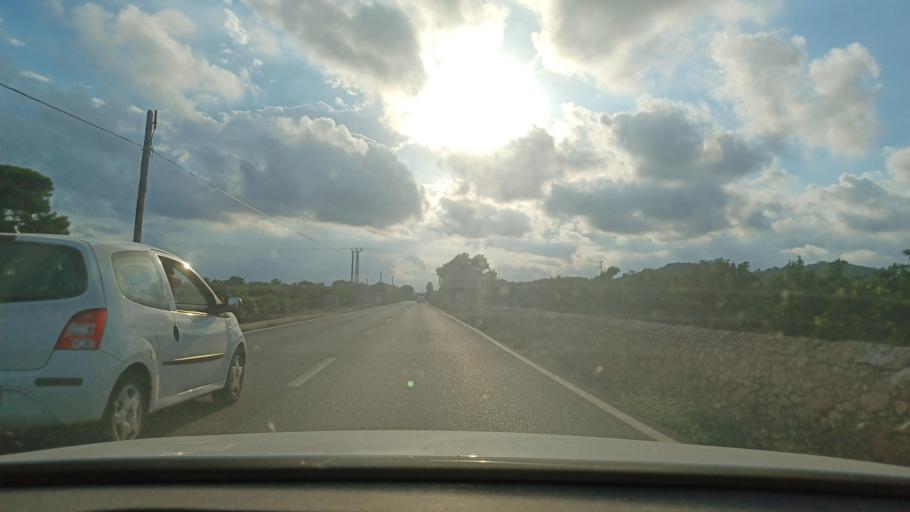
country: ES
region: Catalonia
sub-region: Provincia de Tarragona
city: Alcanar
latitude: 40.5467
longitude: 0.5024
